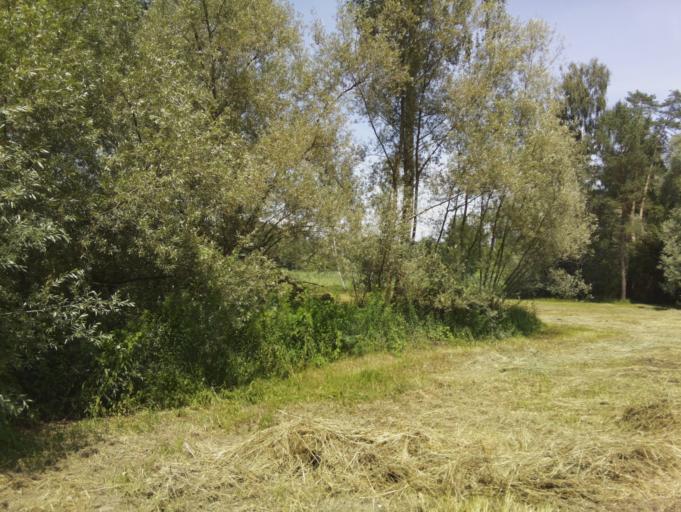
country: CH
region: Zurich
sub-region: Bezirk Andelfingen
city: Kleinandelfingen
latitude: 47.6197
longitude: 8.7093
